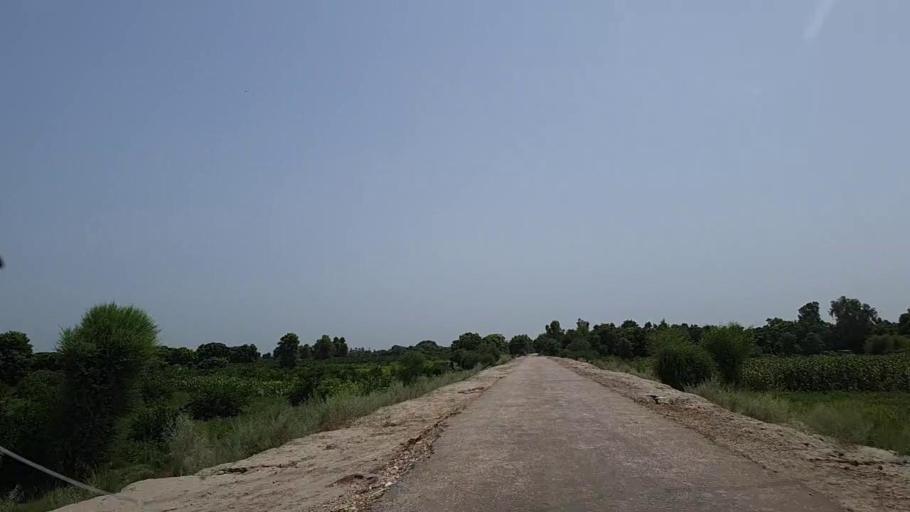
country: PK
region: Sindh
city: Kandiaro
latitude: 27.0505
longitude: 68.1341
